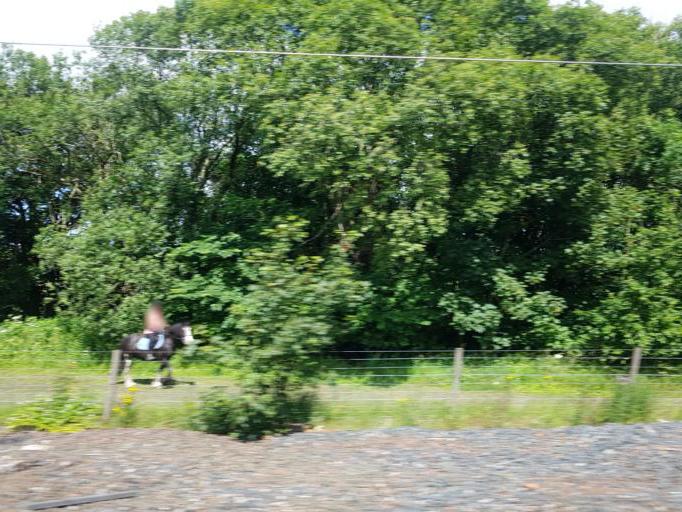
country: GB
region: Scotland
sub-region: Falkirk
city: Bonnybridge
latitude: 55.9844
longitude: -3.9105
